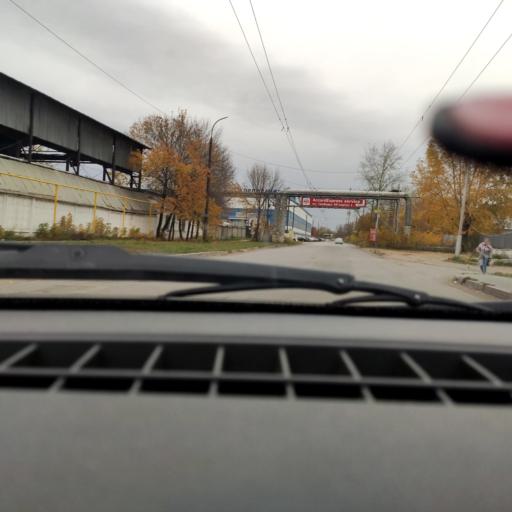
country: RU
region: Bashkortostan
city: Ufa
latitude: 54.8279
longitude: 56.1153
